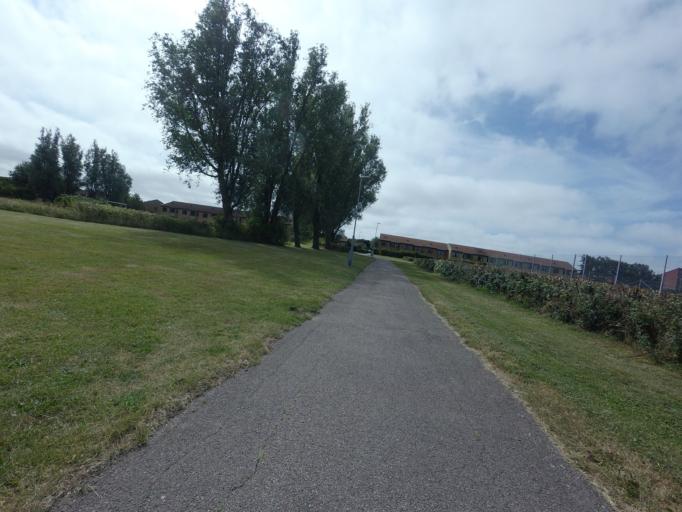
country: SE
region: Skane
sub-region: Hoganas Kommun
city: Hoganas
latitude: 56.1772
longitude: 12.5678
